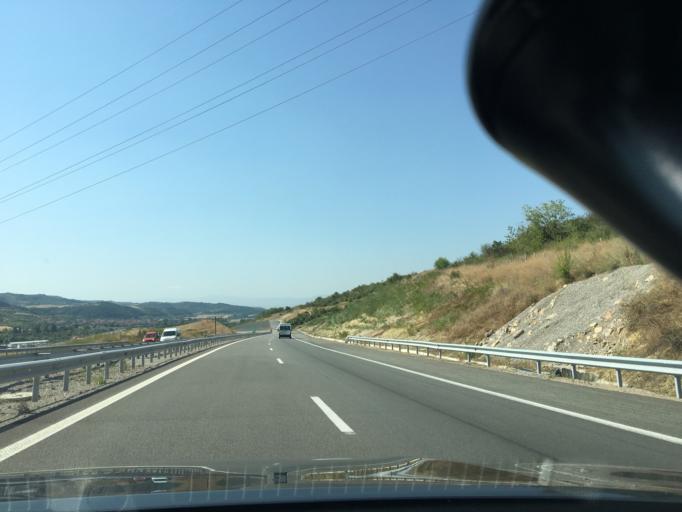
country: BG
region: Kyustendil
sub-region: Obshtina Dupnitsa
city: Dupnitsa
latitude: 42.2479
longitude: 23.0851
